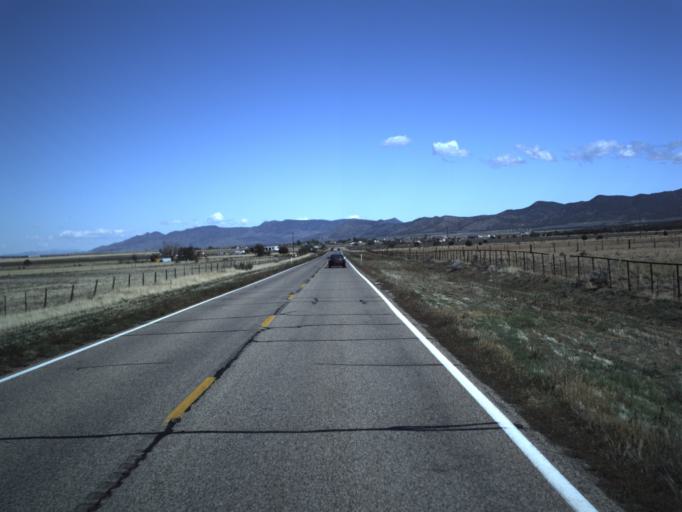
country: US
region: Utah
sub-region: Washington County
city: Enterprise
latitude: 37.5827
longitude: -113.6846
